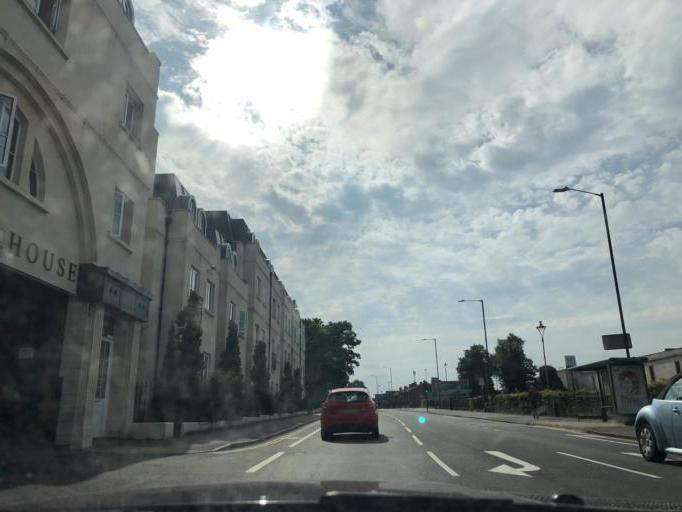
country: GB
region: England
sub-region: Warwickshire
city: Royal Leamington Spa
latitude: 52.2841
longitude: -1.5350
